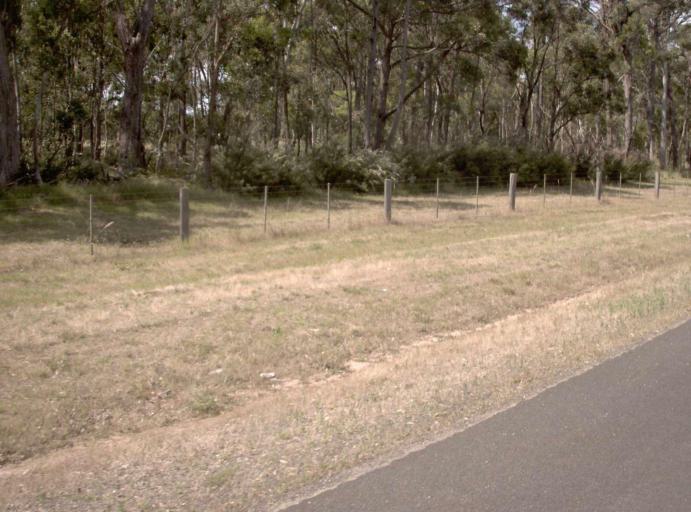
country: AU
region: Victoria
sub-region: Wellington
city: Sale
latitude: -37.9225
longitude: 147.2436
